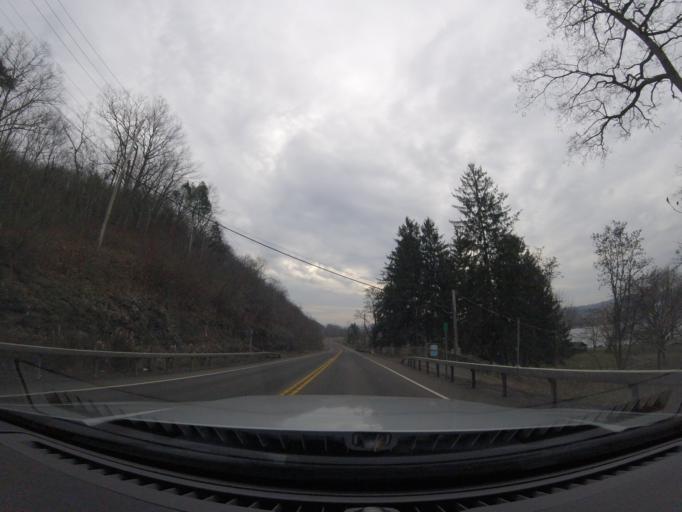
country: US
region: New York
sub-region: Schuyler County
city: Watkins Glen
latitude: 42.3913
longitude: -76.8559
